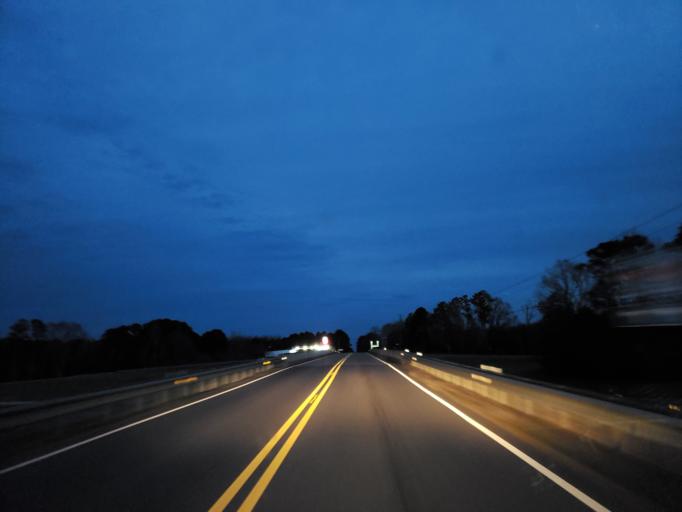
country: US
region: Alabama
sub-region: Greene County
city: Eutaw
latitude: 32.8692
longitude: -87.9250
